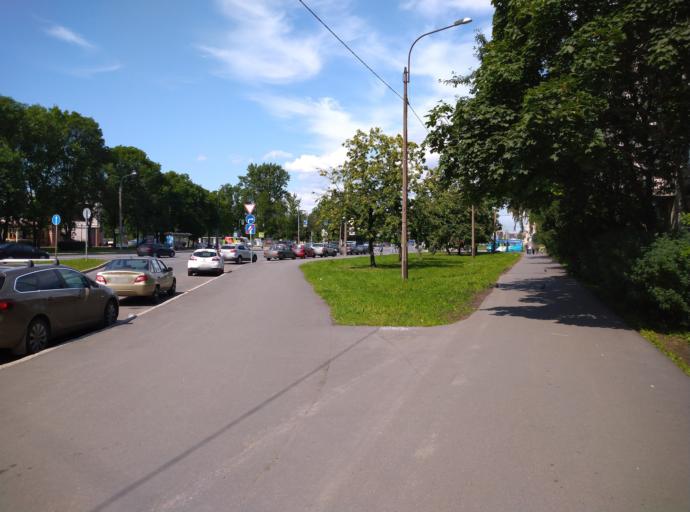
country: RU
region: St.-Petersburg
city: Kupchino
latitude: 59.8635
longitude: 30.3378
